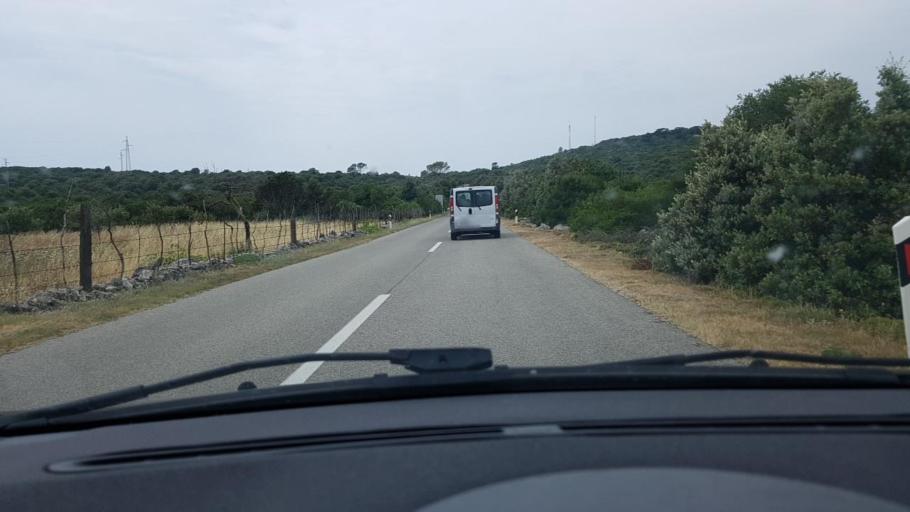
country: HR
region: Dubrovacko-Neretvanska
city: Smokvica
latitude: 42.9487
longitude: 16.9887
